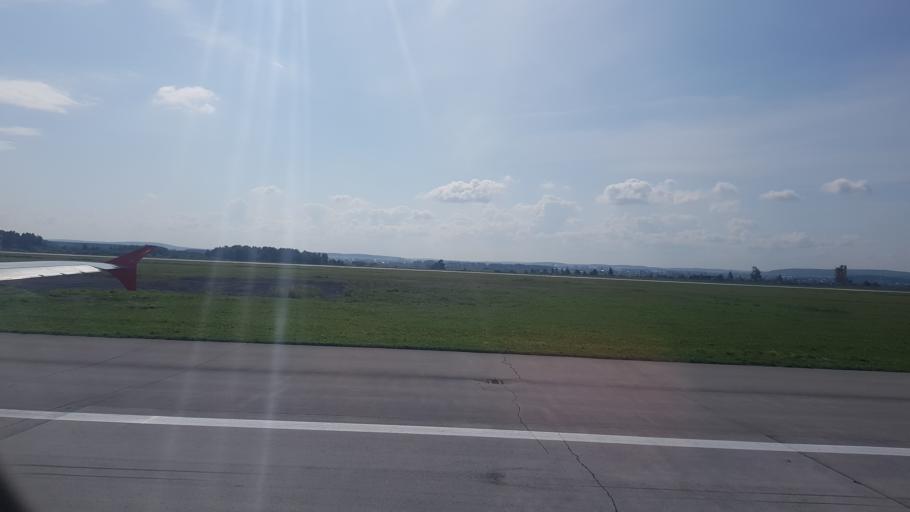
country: RU
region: Sverdlovsk
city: Aramil
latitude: 56.7448
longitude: 60.8115
